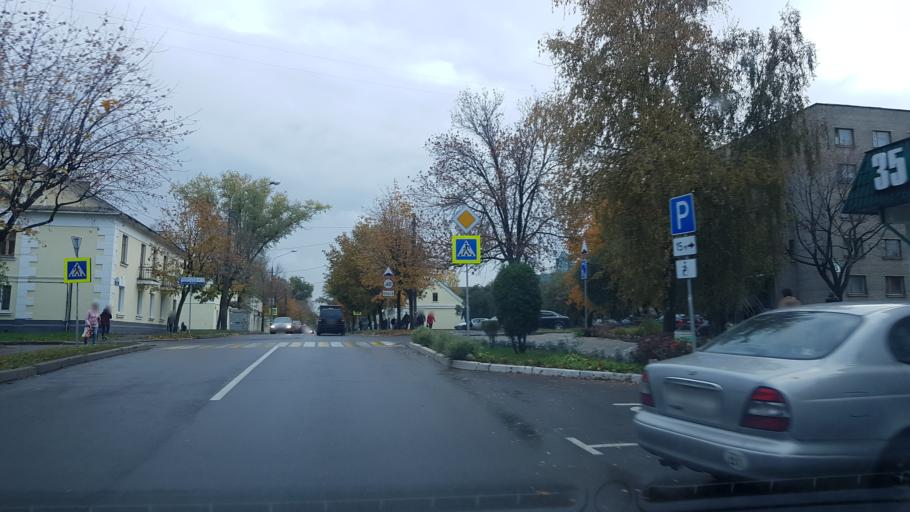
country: BY
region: Minsk
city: Syenitsa
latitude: 53.8478
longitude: 27.5500
